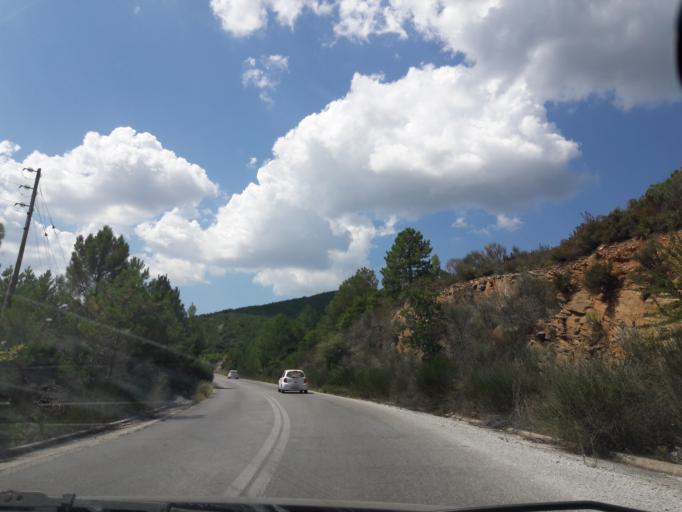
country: GR
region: Central Macedonia
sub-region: Nomos Chalkidikis
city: Polygyros
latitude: 40.3631
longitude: 23.4961
